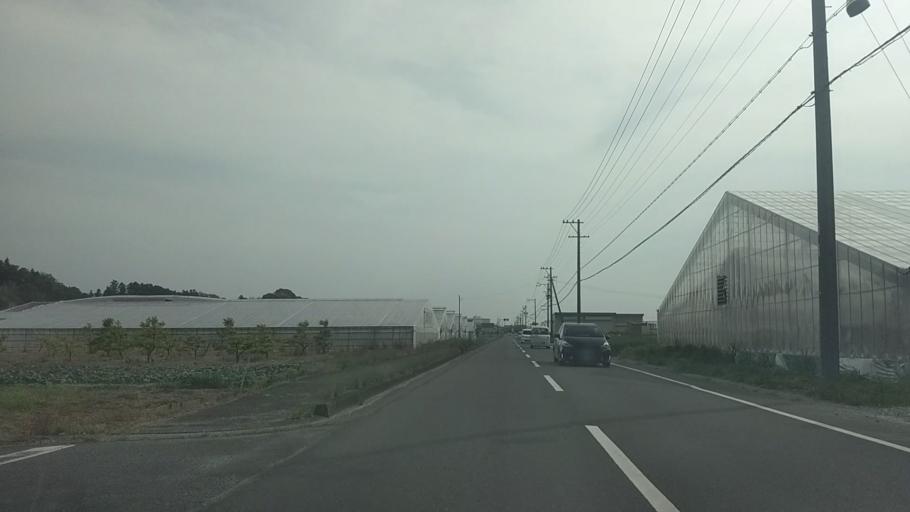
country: JP
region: Shizuoka
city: Kosai-shi
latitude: 34.7225
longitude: 137.6287
